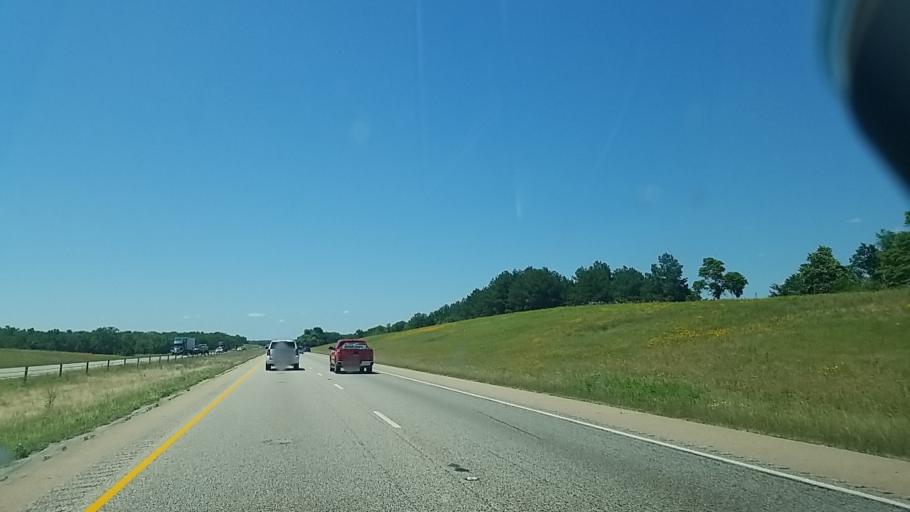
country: US
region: Texas
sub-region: Leon County
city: Buffalo
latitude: 31.3916
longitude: -96.0293
